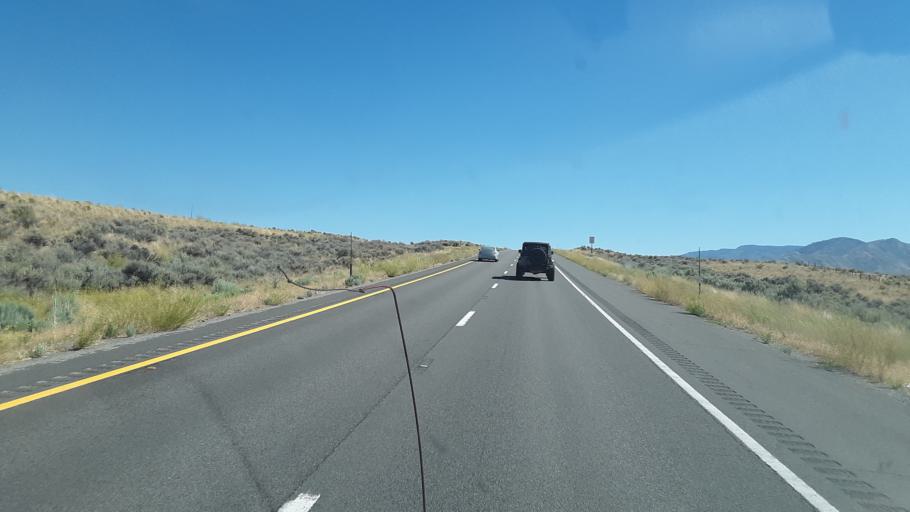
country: US
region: Nevada
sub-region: Washoe County
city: Cold Springs
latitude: 39.7640
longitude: -120.0392
